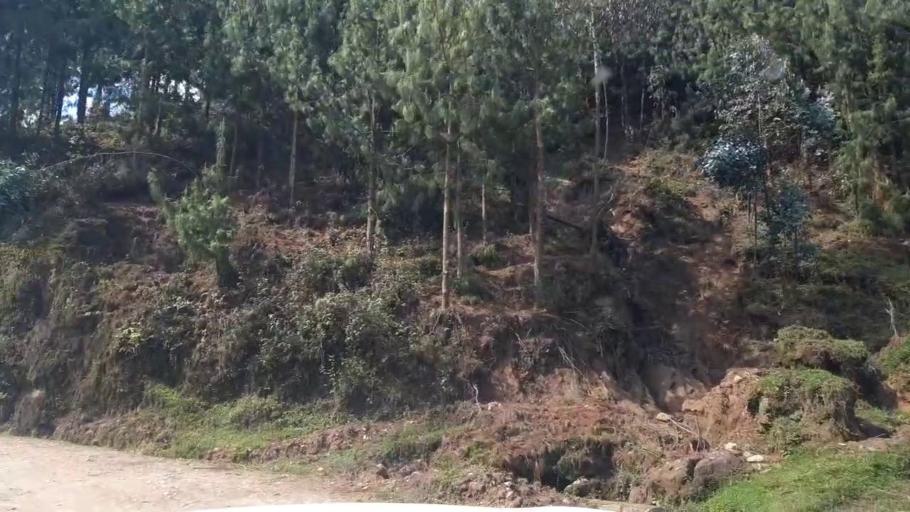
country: RW
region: Western Province
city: Kibuye
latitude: -1.8847
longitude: 29.4691
